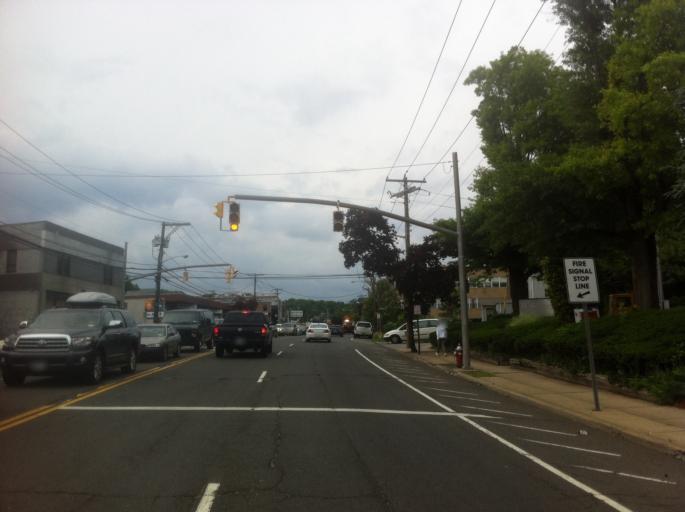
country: US
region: New York
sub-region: Nassau County
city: Roslyn Heights
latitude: 40.7863
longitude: -73.6492
